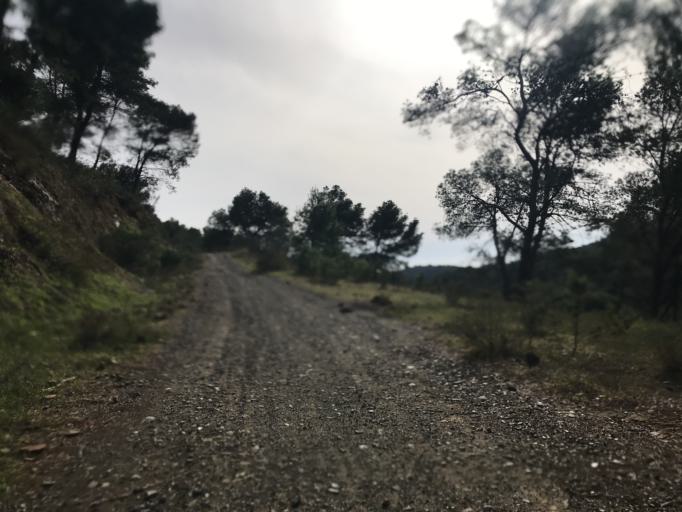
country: ES
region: Andalusia
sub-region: Provincia de Malaga
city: Malaga
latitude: 36.8049
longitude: -4.4036
